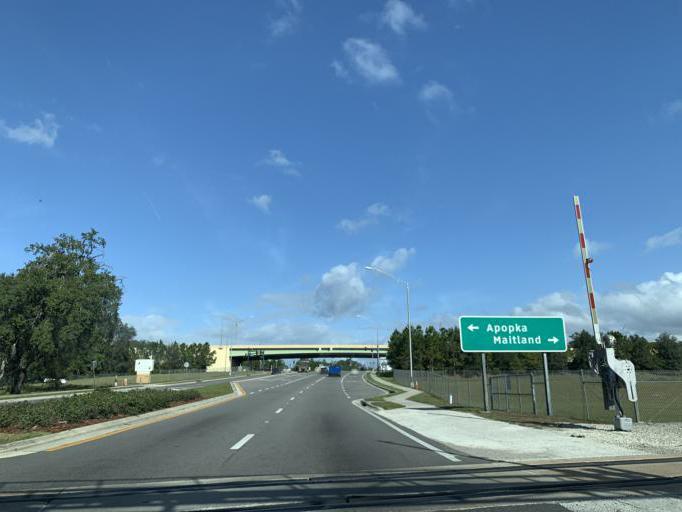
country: US
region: Florida
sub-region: Orange County
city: Clarcona
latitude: 28.6322
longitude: -81.4764
